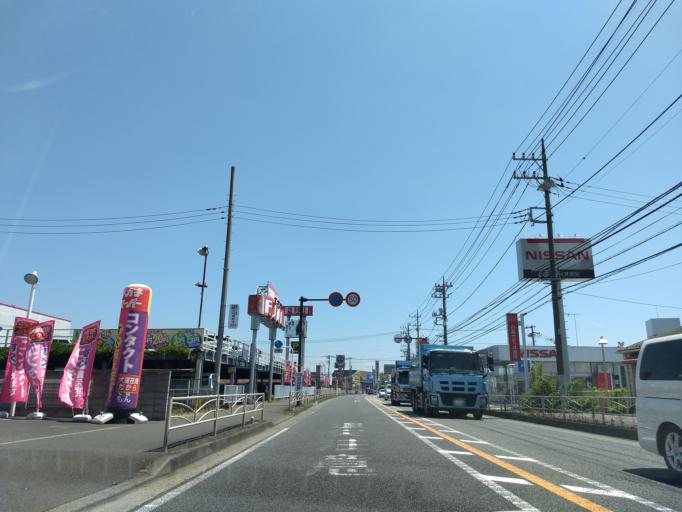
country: JP
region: Kanagawa
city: Isehara
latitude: 35.3970
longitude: 139.2926
